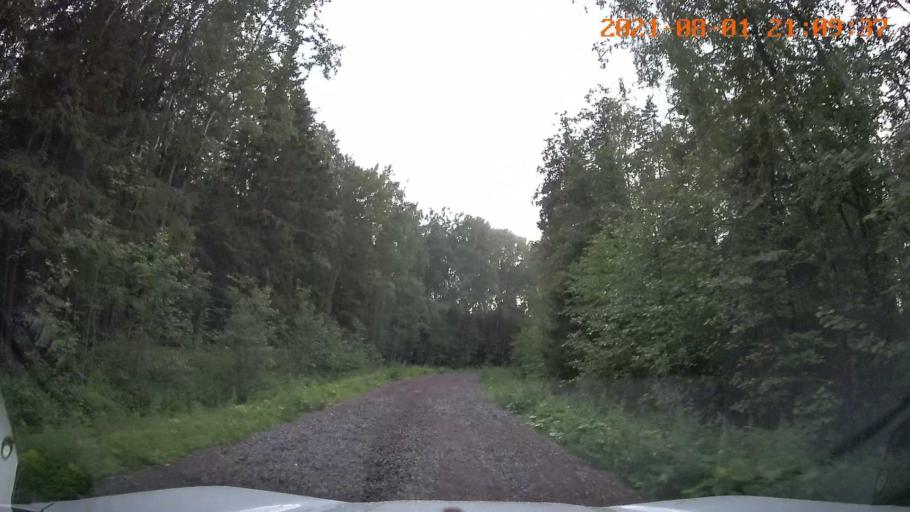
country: RU
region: Leningrad
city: Syas'stroy
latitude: 60.5118
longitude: 32.6460
